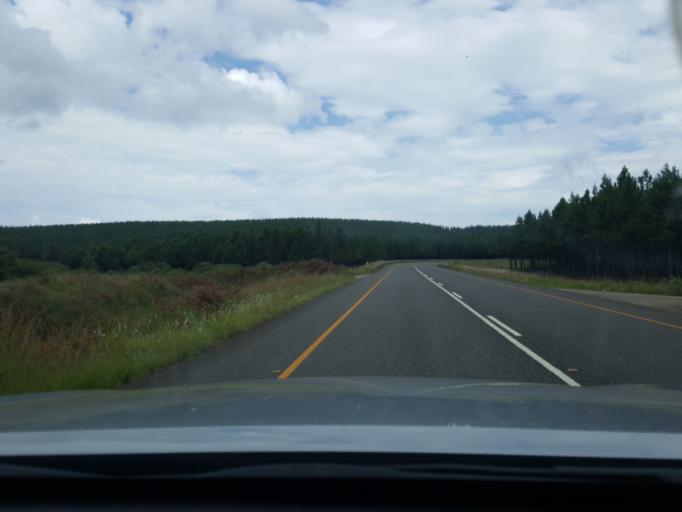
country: ZA
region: Mpumalanga
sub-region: Ehlanzeni District
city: Graksop
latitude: -25.1592
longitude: 30.8394
